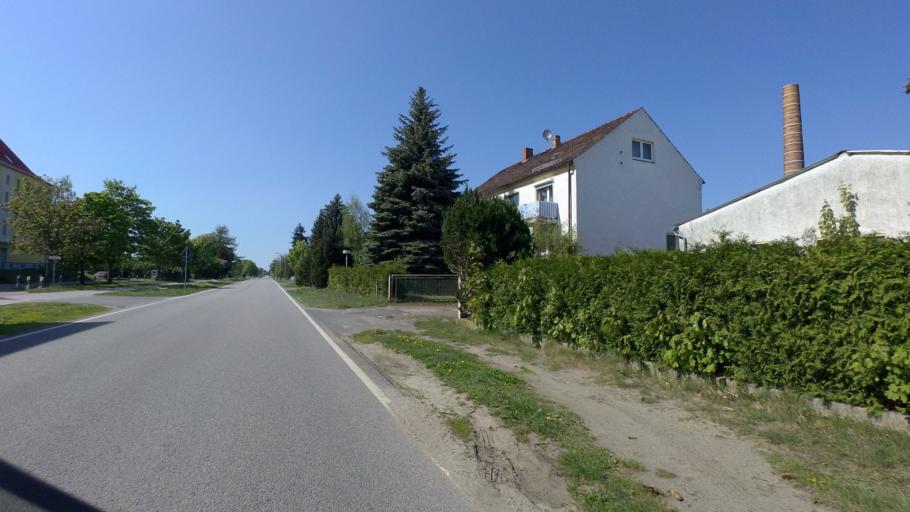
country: DE
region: Brandenburg
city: Schlepzig
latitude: 52.0441
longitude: 14.0239
